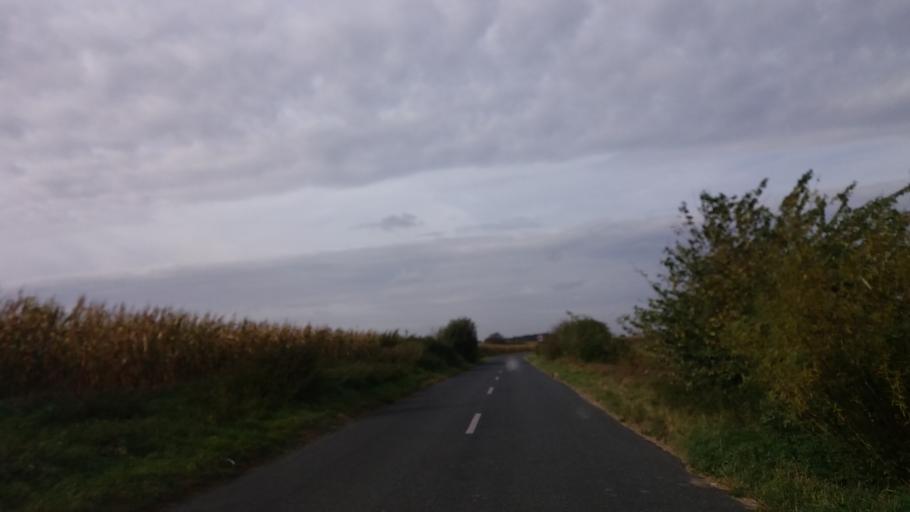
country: PL
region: West Pomeranian Voivodeship
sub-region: Powiat choszczenski
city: Krzecin
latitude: 53.0395
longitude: 15.4965
